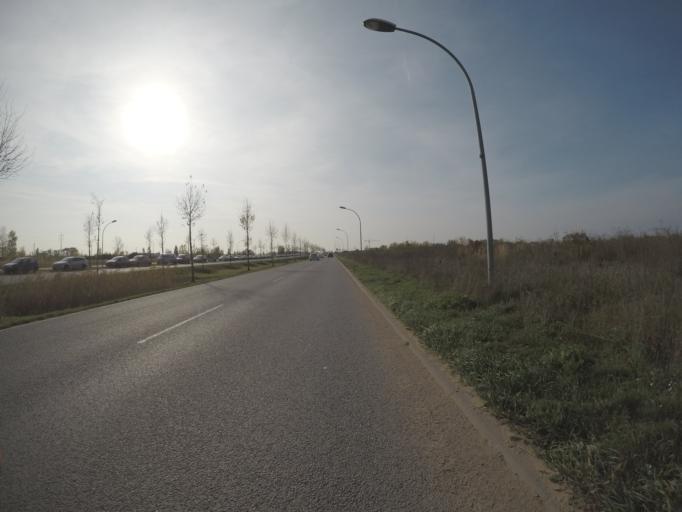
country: DE
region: Brandenburg
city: Schonefeld
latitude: 52.3953
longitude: 13.5142
